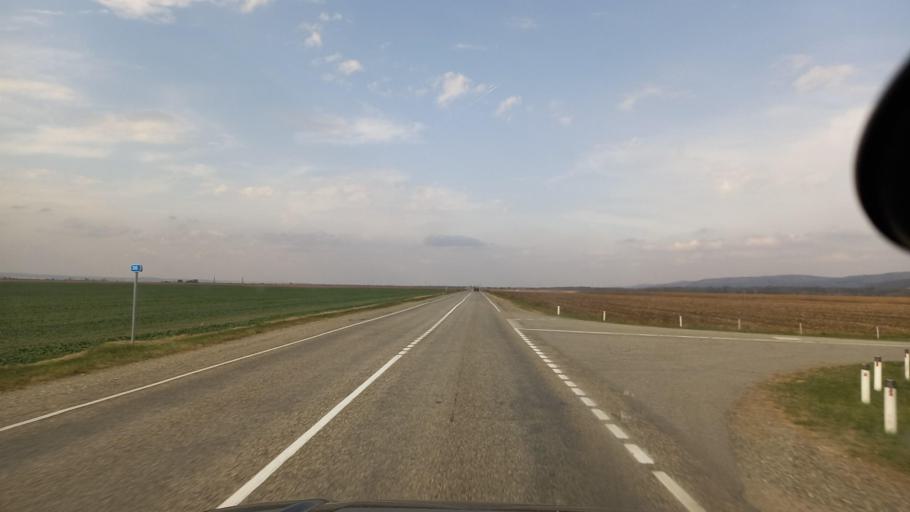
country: RU
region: Krasnodarskiy
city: Perepravnaya
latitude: 44.3101
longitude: 40.8574
